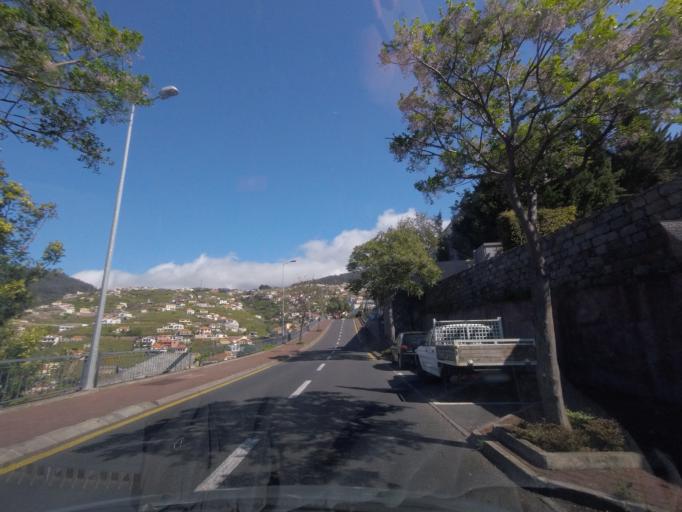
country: PT
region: Madeira
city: Camara de Lobos
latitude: 32.6699
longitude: -16.9801
